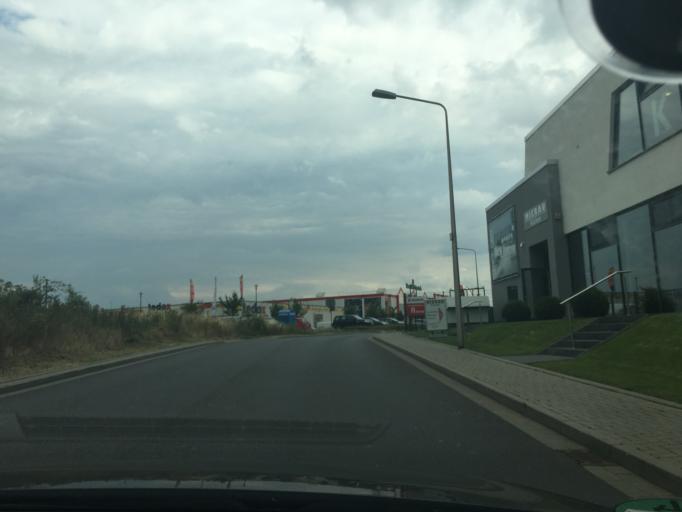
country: DE
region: North Rhine-Westphalia
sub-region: Regierungsbezirk Koln
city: Dueren
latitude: 50.8310
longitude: 6.4734
